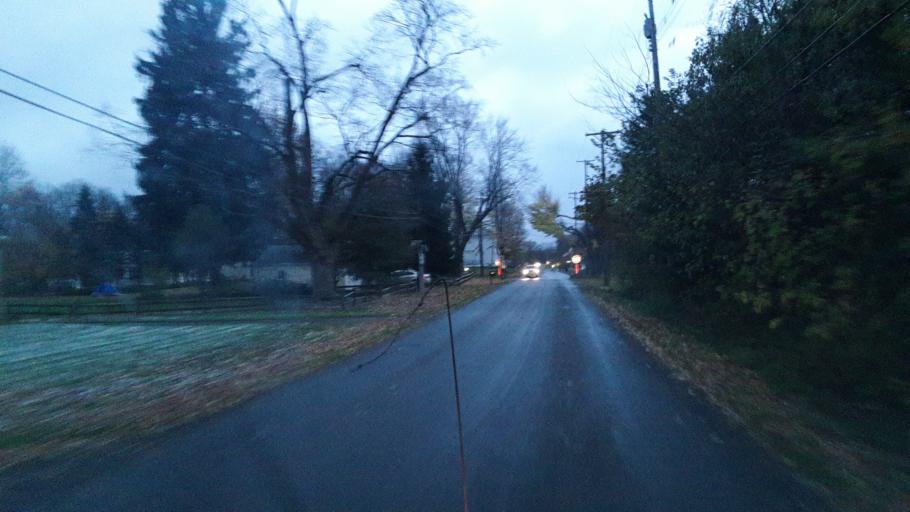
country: US
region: Ohio
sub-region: Portage County
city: Mantua
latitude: 41.3109
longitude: -81.2447
